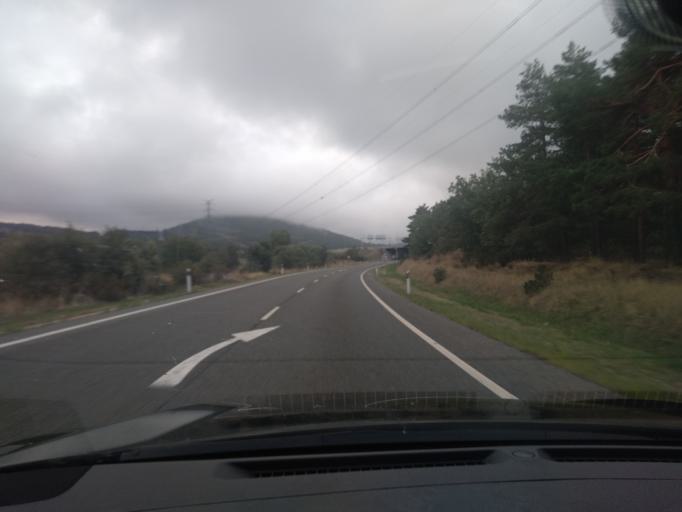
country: ES
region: Castille and Leon
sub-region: Provincia de Segovia
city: Otero de Herreros
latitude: 40.7361
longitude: -4.2017
